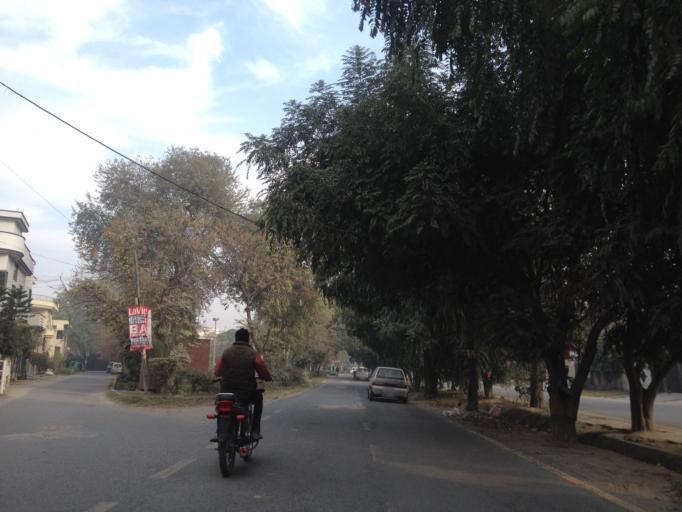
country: PK
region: Punjab
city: Lahore
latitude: 31.4661
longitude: 74.3022
